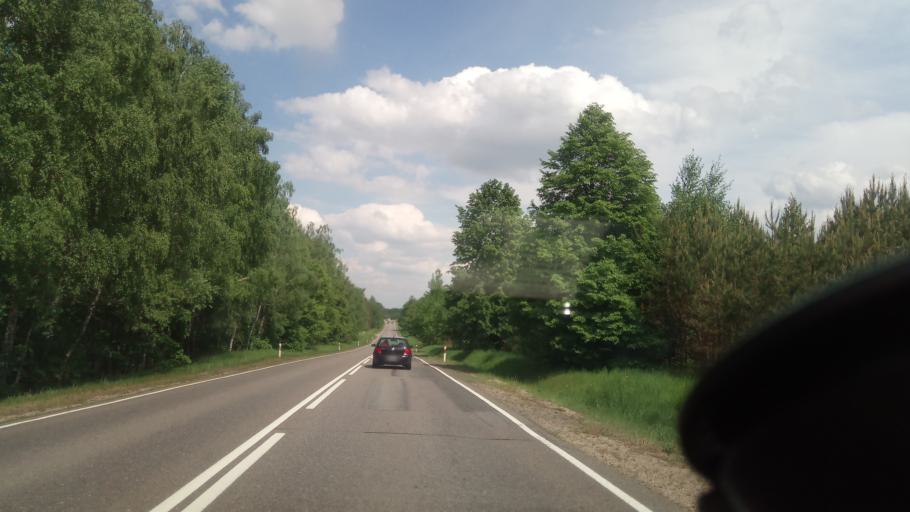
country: LT
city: Trakai
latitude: 54.6082
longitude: 24.8596
